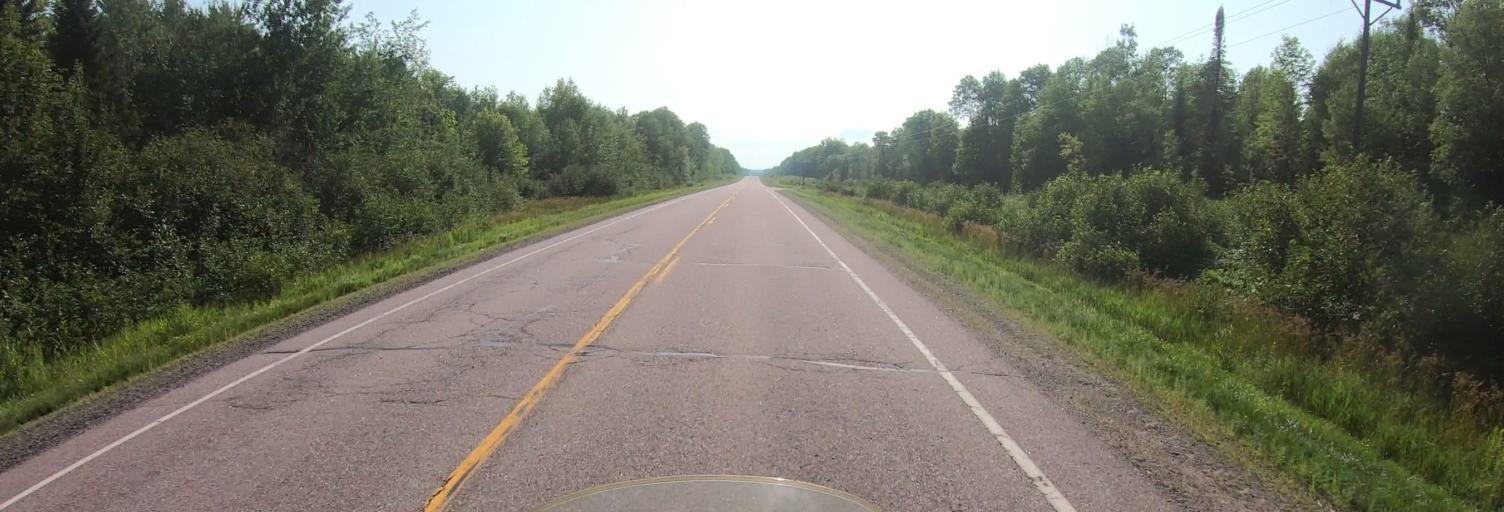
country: US
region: Wisconsin
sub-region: Iron County
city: Hurley
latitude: 46.3625
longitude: -90.4434
